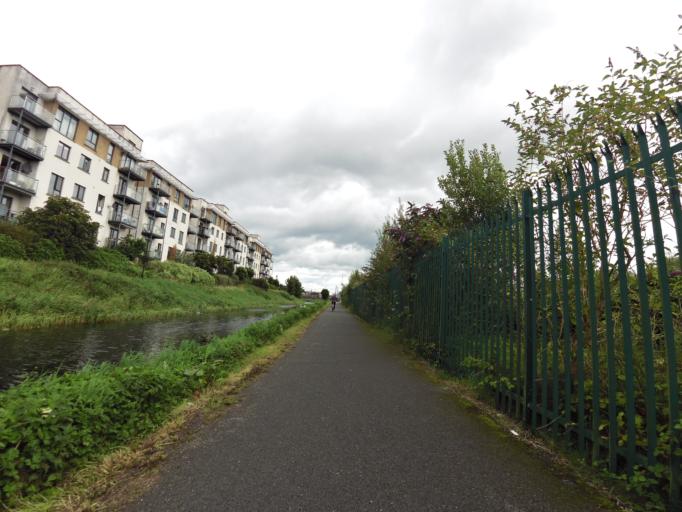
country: IE
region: Leinster
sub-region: An Iarmhi
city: An Muileann gCearr
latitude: 53.5220
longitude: -7.3498
